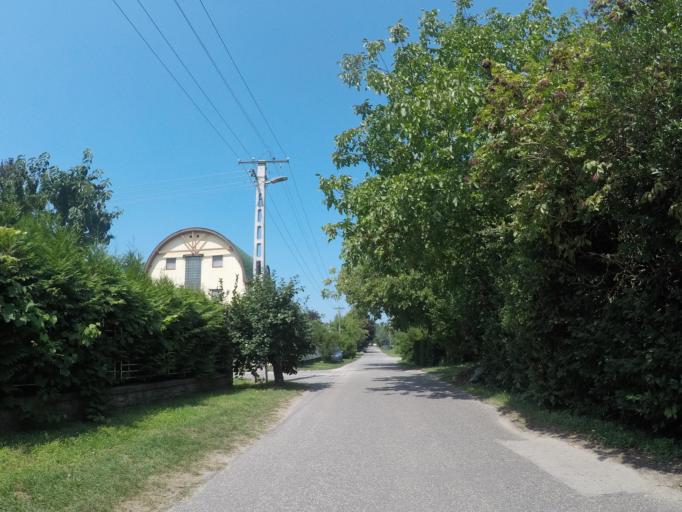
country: HU
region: Somogy
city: Balatonszabadi
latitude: 46.9335
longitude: 18.1233
